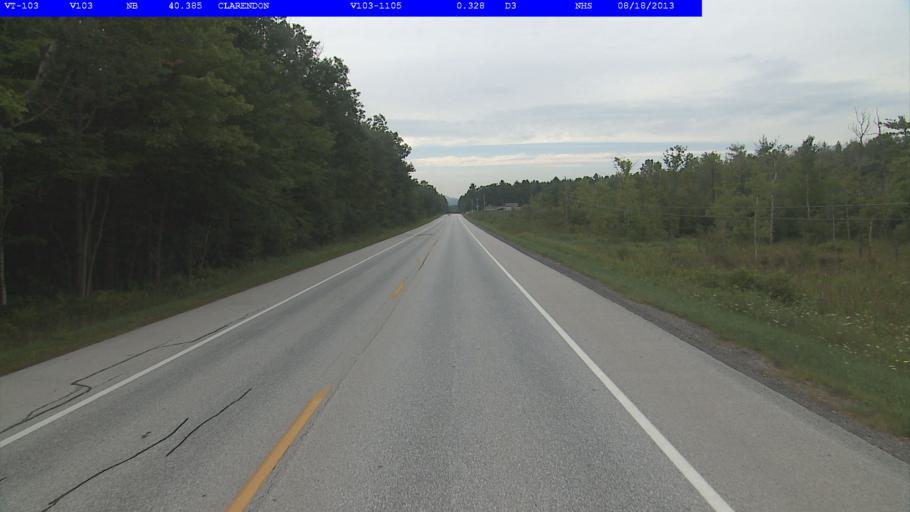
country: US
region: Vermont
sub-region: Rutland County
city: Rutland
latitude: 43.5277
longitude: -72.9345
